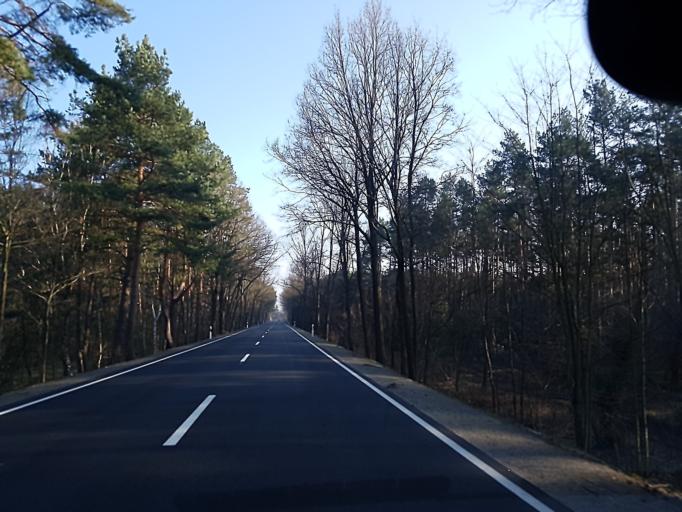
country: DE
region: Brandenburg
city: Bronkow
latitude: 51.6933
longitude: 13.9179
